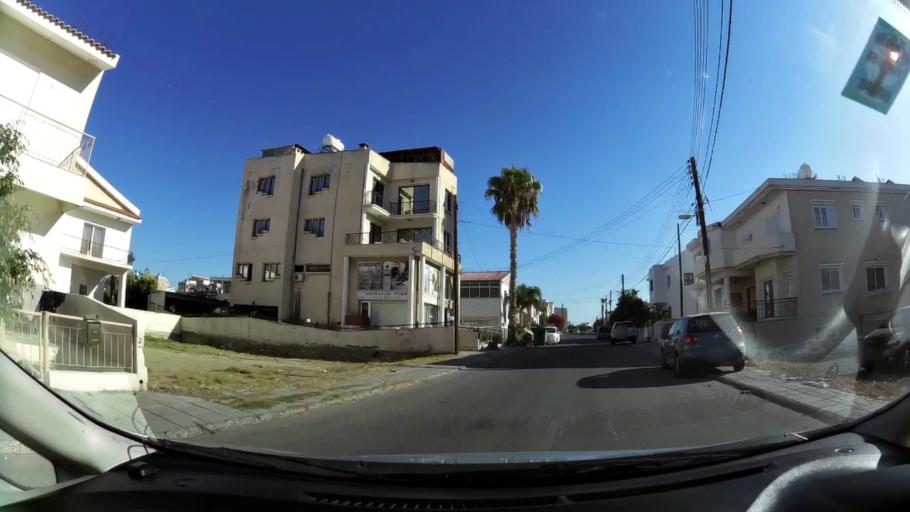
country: CY
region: Larnaka
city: Larnaca
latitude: 34.9282
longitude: 33.6150
